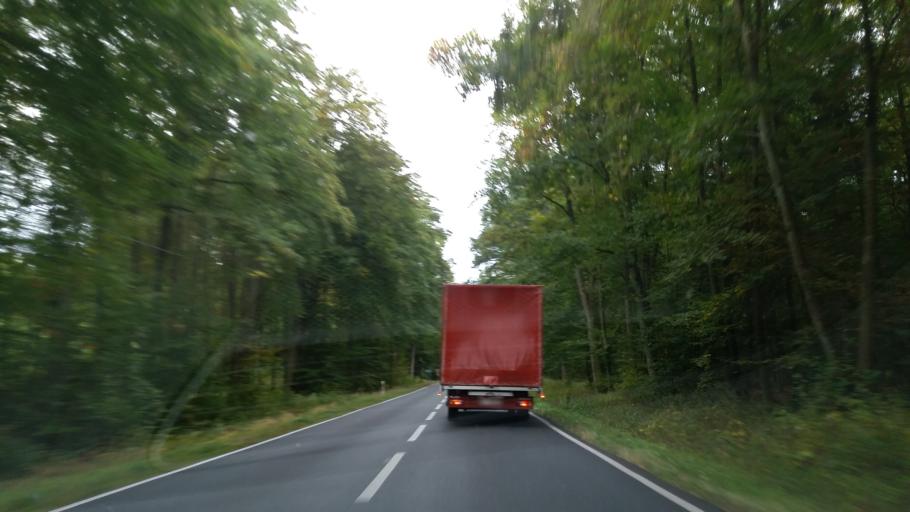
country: PL
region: West Pomeranian Voivodeship
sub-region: Powiat mysliborski
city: Barlinek
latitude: 52.9378
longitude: 15.1918
